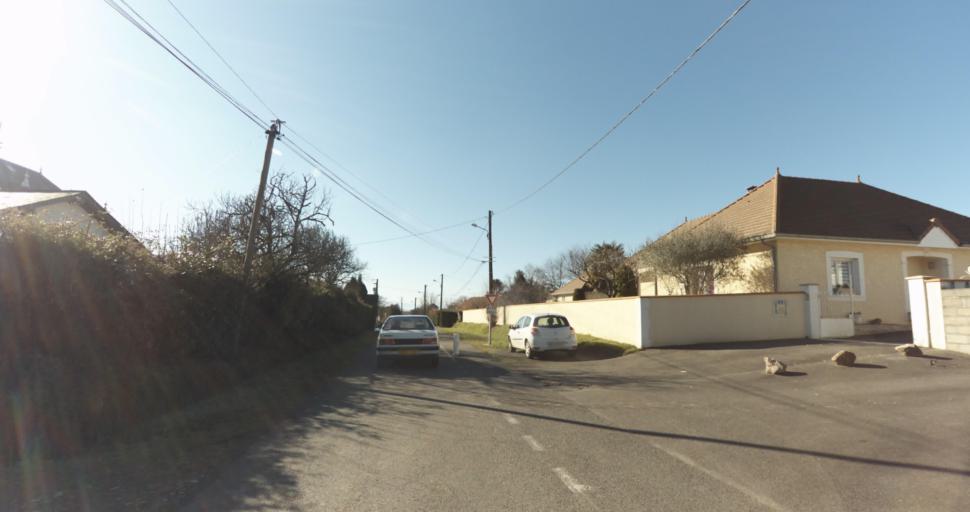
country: FR
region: Aquitaine
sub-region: Departement des Pyrenees-Atlantiques
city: Morlaas
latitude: 43.3385
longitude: -0.2715
